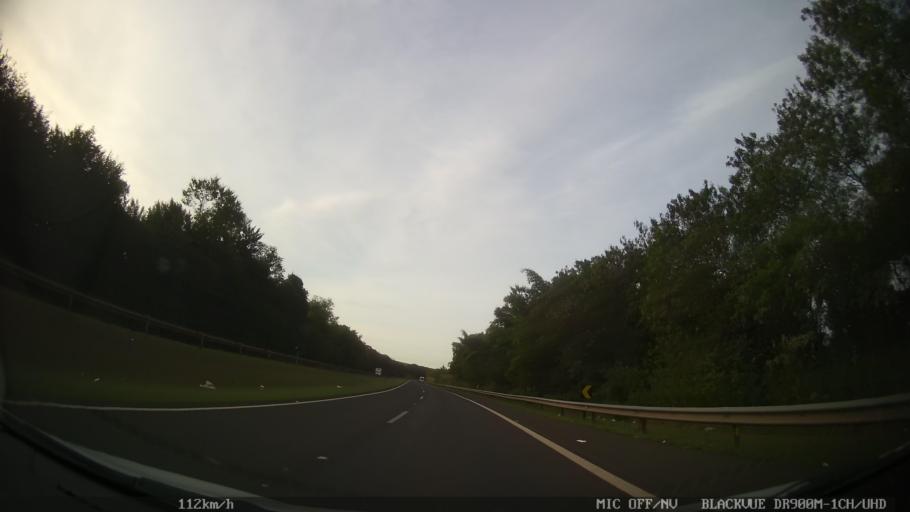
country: BR
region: Sao Paulo
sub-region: Piracicaba
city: Piracicaba
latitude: -22.6962
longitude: -47.5916
